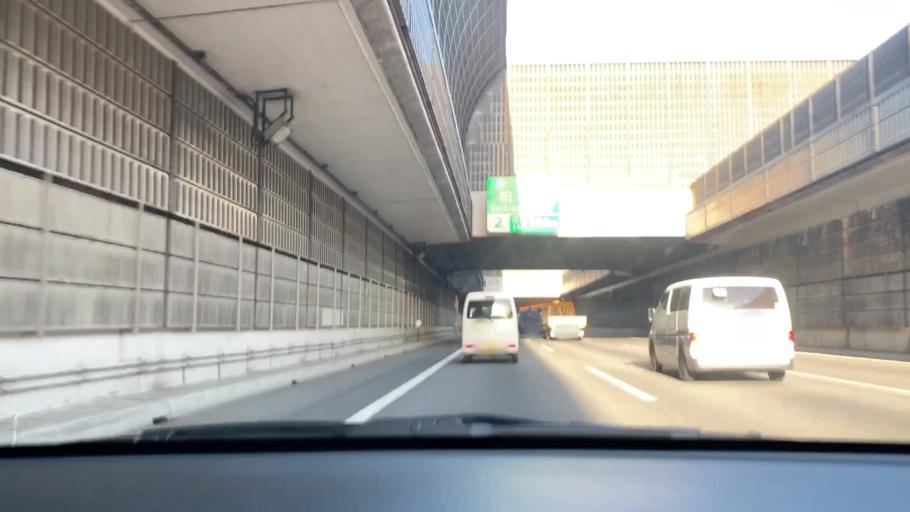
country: JP
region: Chiba
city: Nagareyama
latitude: 35.9010
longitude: 139.9266
